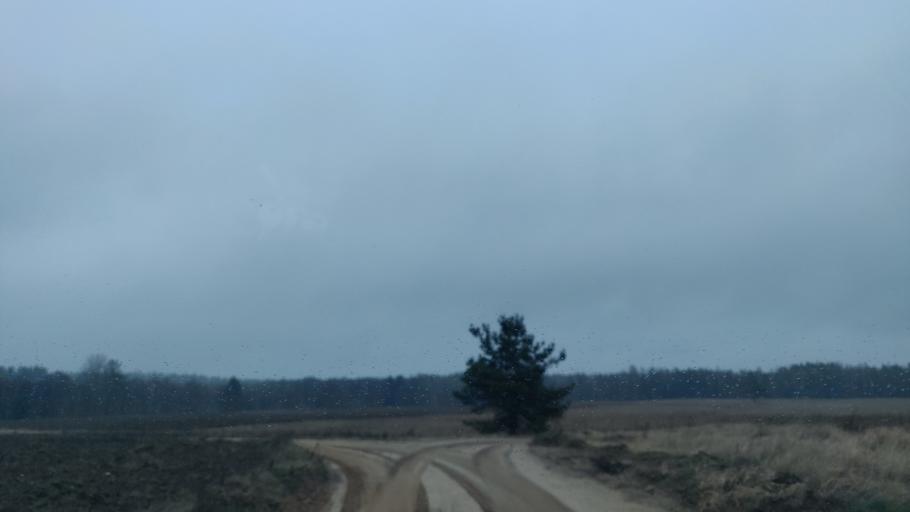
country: LT
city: Trakai
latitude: 54.5623
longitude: 24.9297
